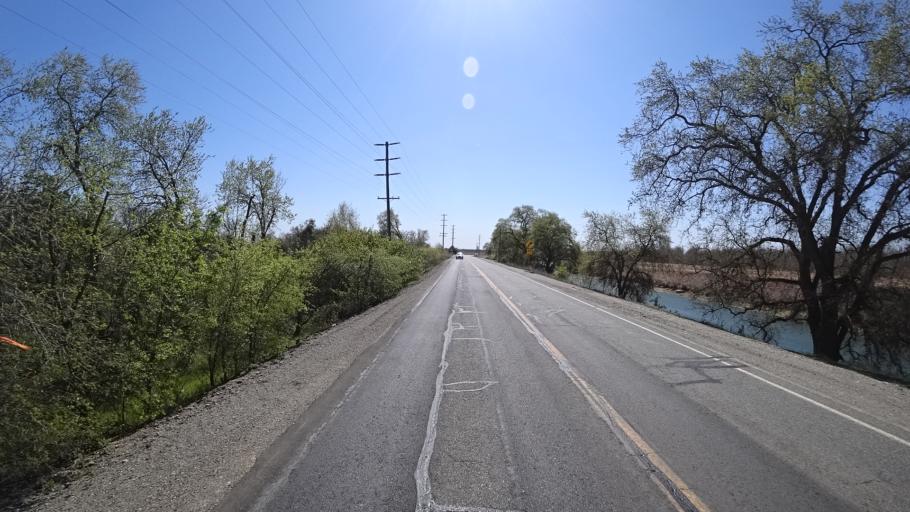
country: US
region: California
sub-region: Glenn County
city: Hamilton City
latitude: 39.7660
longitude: -122.0304
